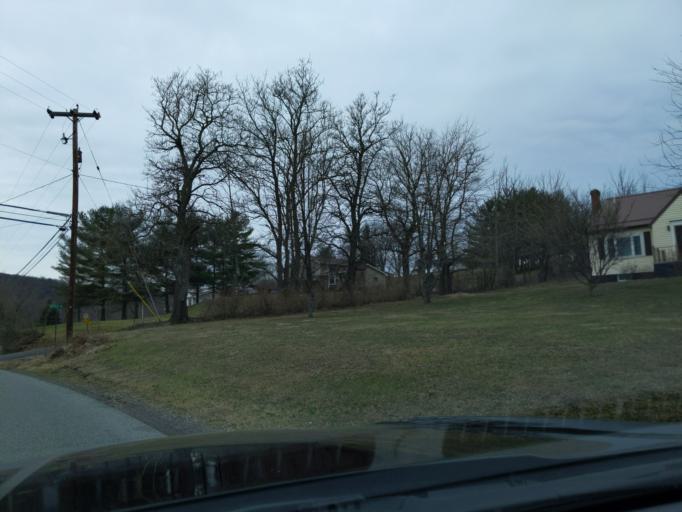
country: US
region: Pennsylvania
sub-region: Blair County
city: Greenwood
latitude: 40.5793
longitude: -78.3747
